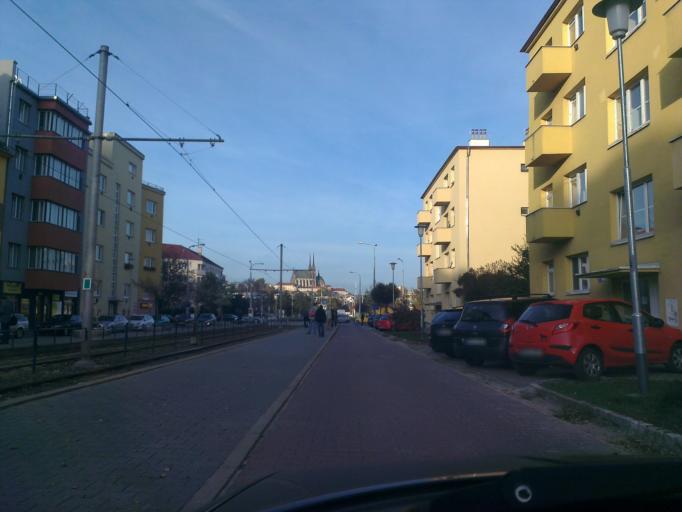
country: CZ
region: South Moravian
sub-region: Mesto Brno
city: Brno
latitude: 49.1821
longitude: 16.6003
